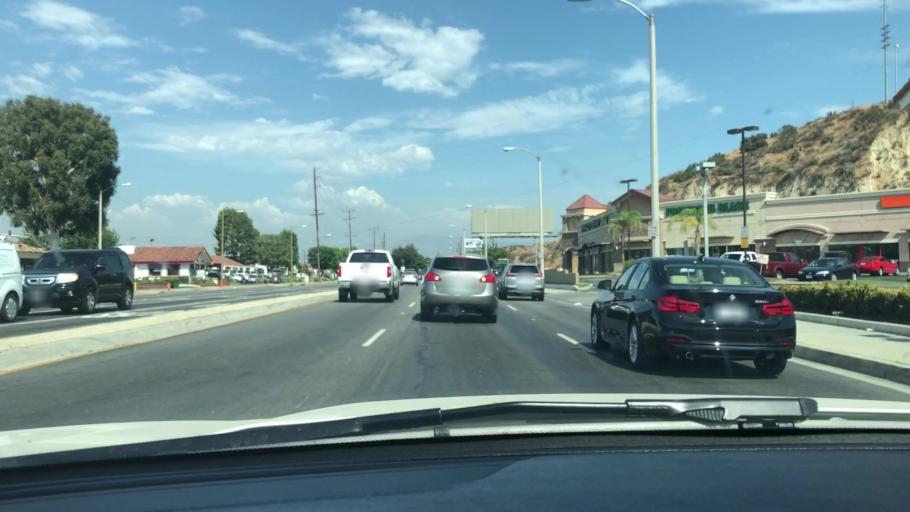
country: US
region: California
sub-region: Los Angeles County
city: Santa Clarita
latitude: 34.4225
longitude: -118.5407
